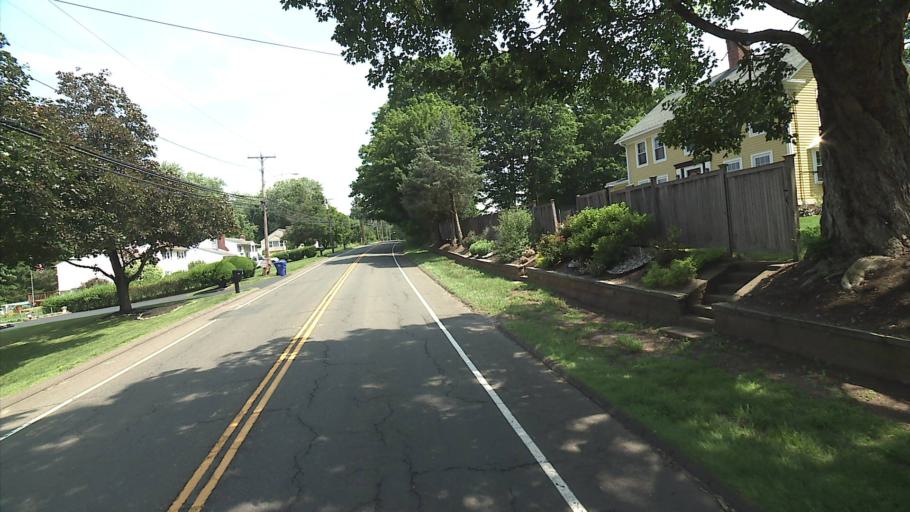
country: US
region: Connecticut
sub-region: New Haven County
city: North Branford
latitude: 41.3126
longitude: -72.7710
